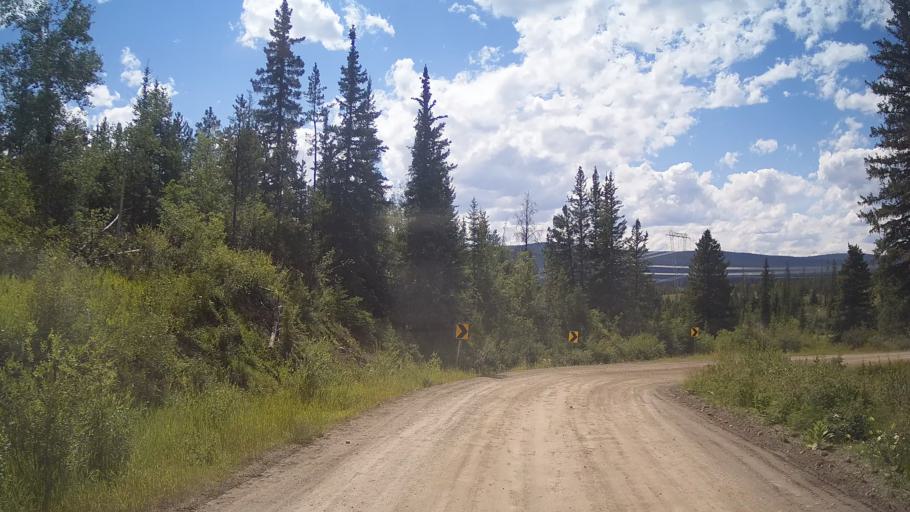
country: CA
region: British Columbia
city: Lillooet
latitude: 51.3369
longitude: -121.9580
